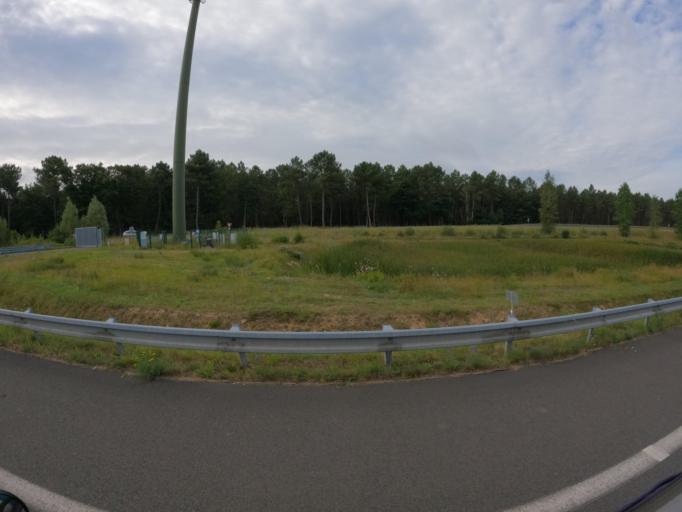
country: FR
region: Centre
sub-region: Departement d'Indre-et-Loire
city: Langeais
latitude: 47.3466
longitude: 0.3691
